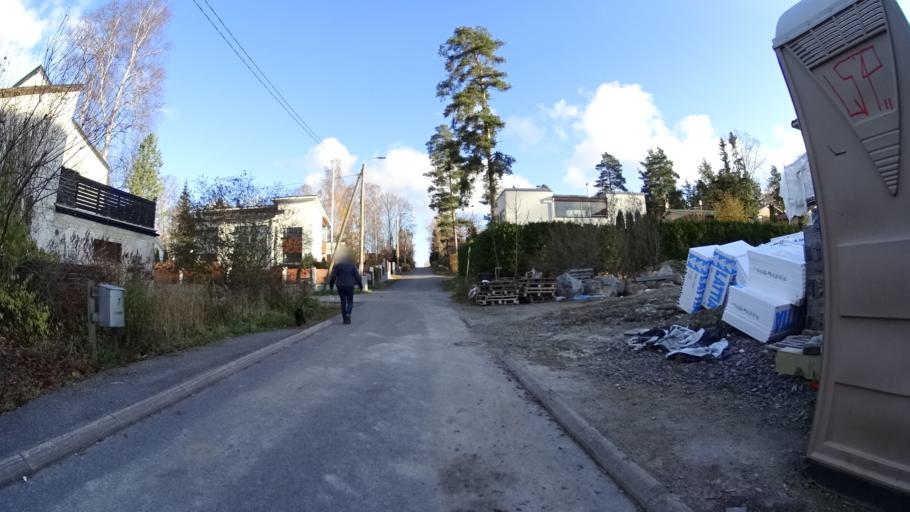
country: FI
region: Uusimaa
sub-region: Helsinki
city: Kilo
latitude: 60.2615
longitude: 24.8257
